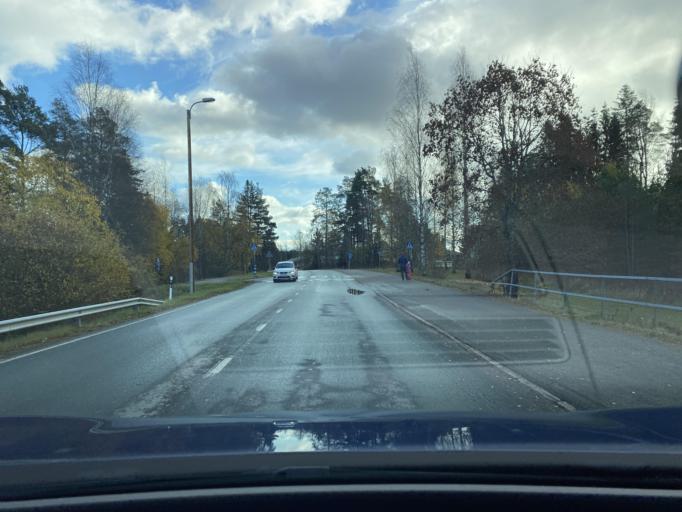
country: FI
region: Varsinais-Suomi
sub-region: Loimaa
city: Aura
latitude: 60.7209
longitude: 22.6006
